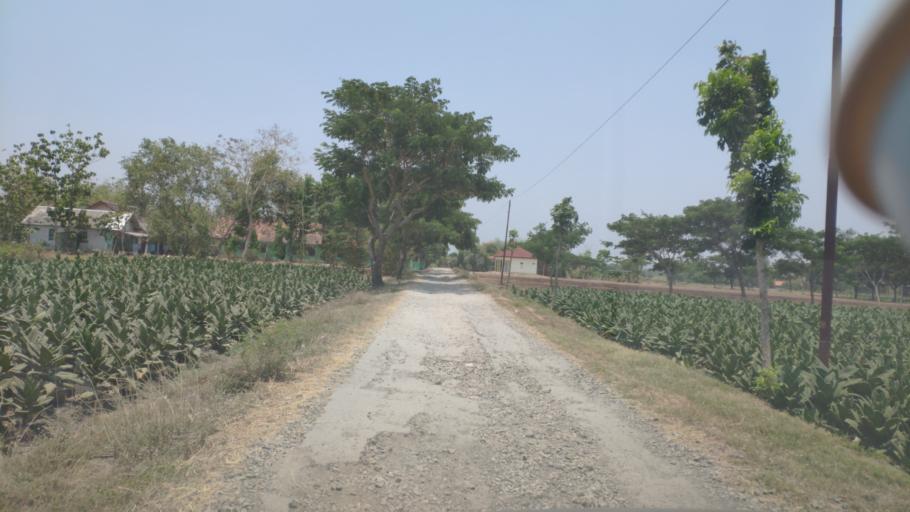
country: ID
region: Central Java
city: Gayam
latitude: -7.2230
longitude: 111.4422
